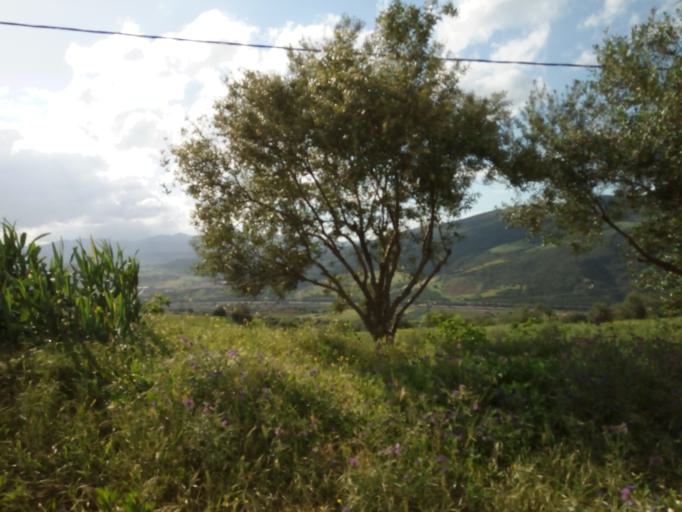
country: DZ
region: Tipaza
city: El Affroun
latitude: 36.3736
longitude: 2.4983
